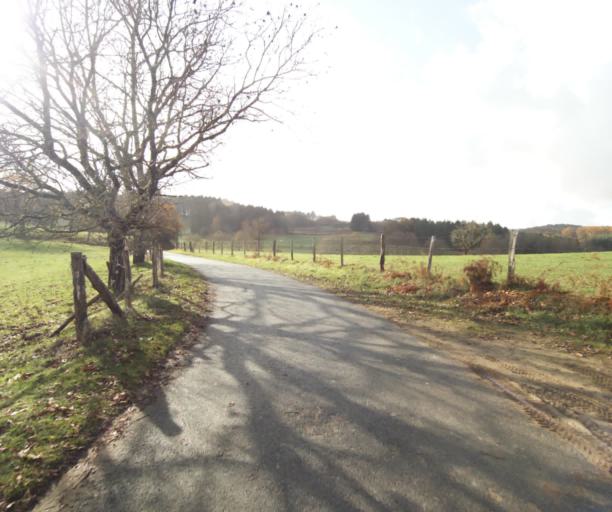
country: FR
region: Limousin
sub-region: Departement de la Correze
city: Chameyrat
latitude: 45.2277
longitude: 1.6865
